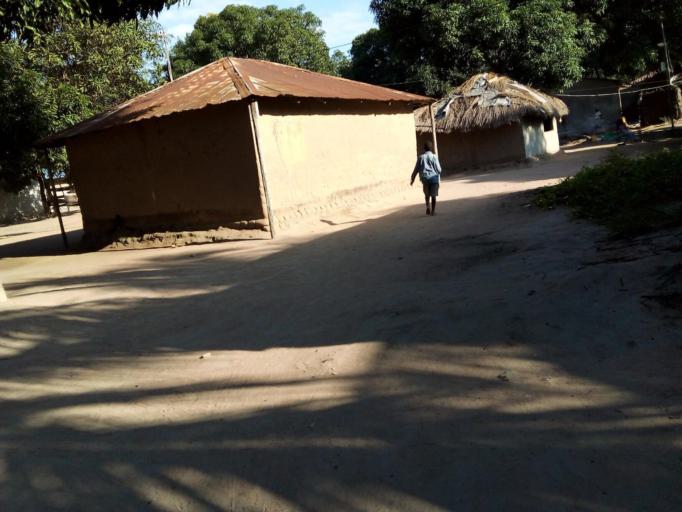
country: MZ
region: Zambezia
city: Quelimane
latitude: -17.6045
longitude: 36.8233
